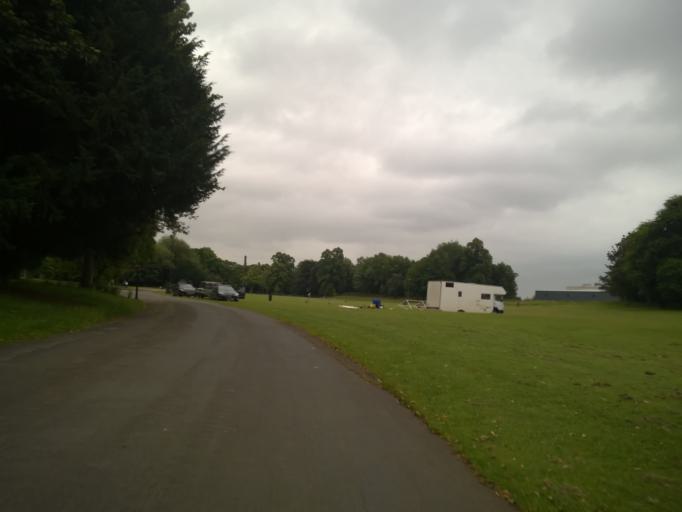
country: GB
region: England
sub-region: City of Leicester
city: Leicester
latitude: 52.6442
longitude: -1.1345
